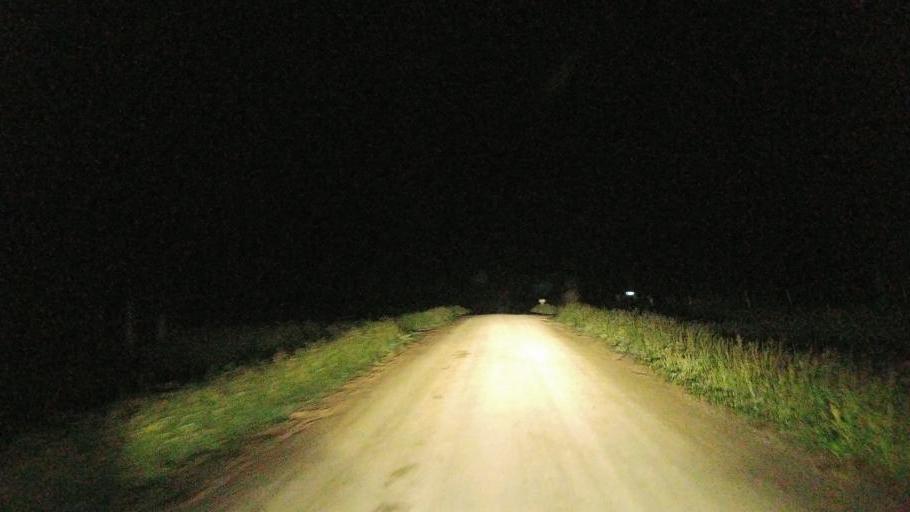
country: US
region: Iowa
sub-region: Decatur County
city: Lamoni
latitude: 40.6242
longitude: -94.0345
